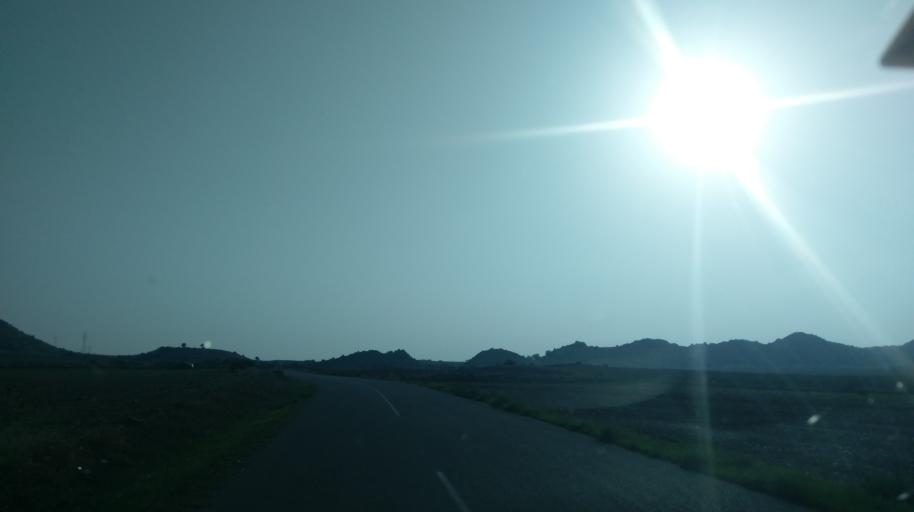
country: CY
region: Ammochostos
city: Leonarisso
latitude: 35.4608
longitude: 34.0974
